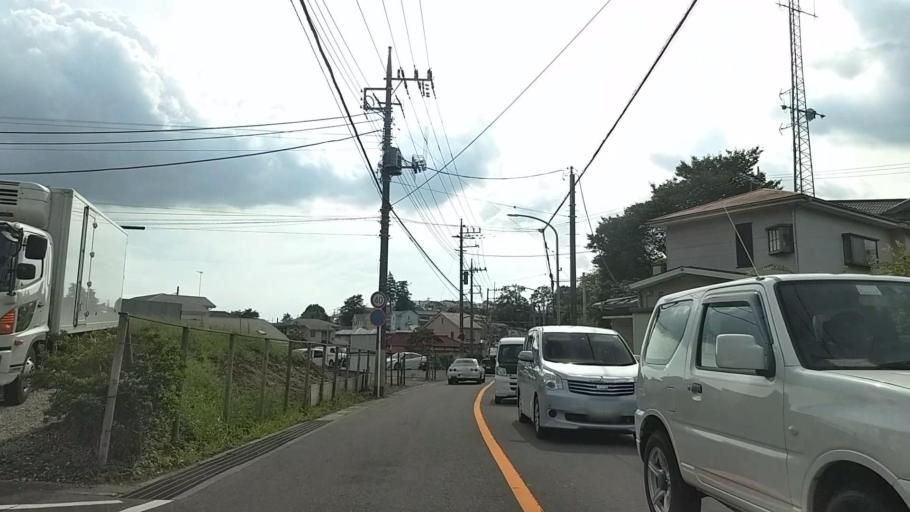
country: JP
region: Kanagawa
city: Yokohama
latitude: 35.4870
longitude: 139.5725
